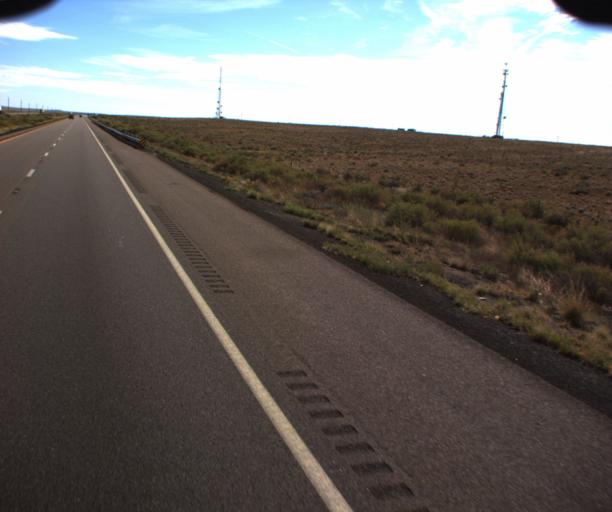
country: US
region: Arizona
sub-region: Navajo County
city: Holbrook
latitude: 35.0180
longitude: -109.8545
